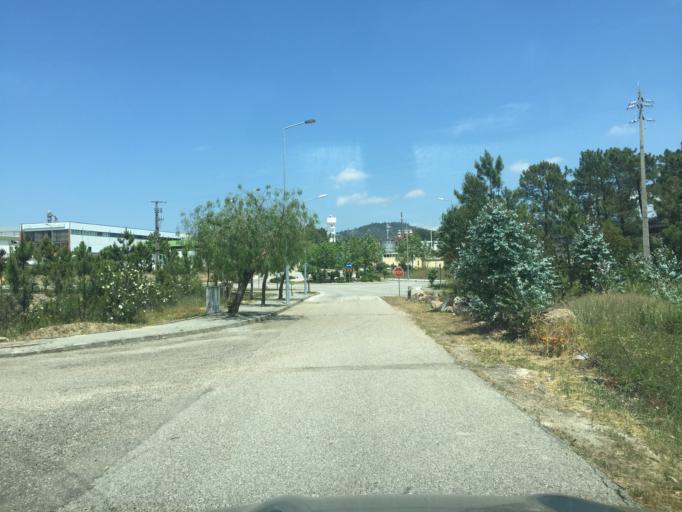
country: PT
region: Castelo Branco
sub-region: Vila de Rei
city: Vila de Rei
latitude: 39.6756
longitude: -8.1401
